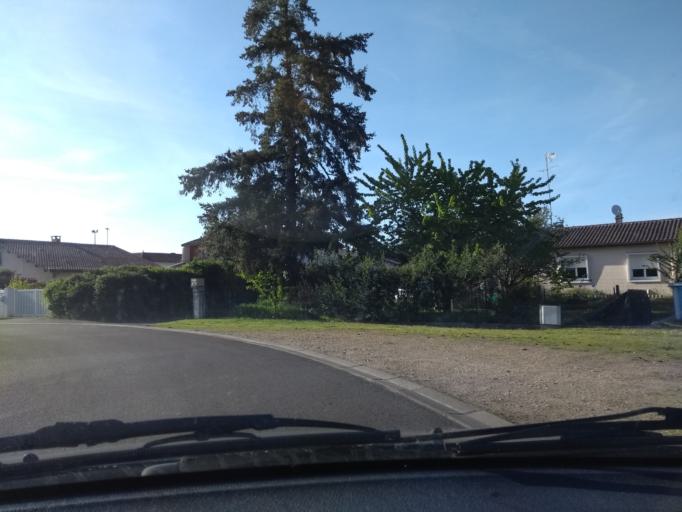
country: FR
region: Aquitaine
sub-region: Departement des Landes
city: Parentis-en-Born
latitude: 44.3551
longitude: -1.0714
